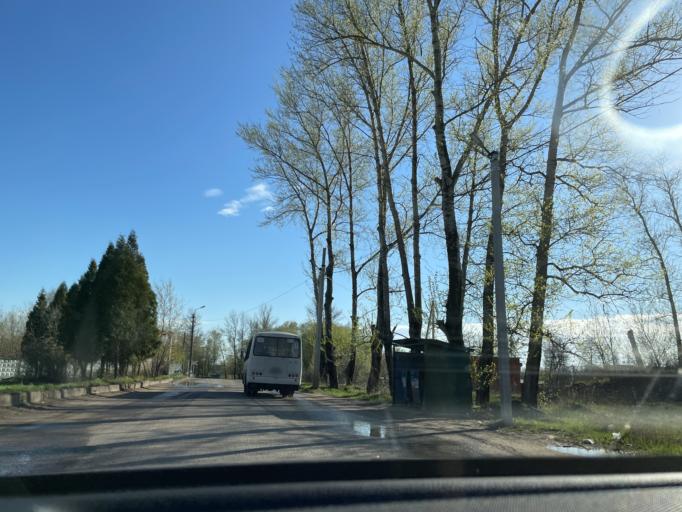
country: RU
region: Tula
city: Aleksin
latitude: 54.4950
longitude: 36.9864
